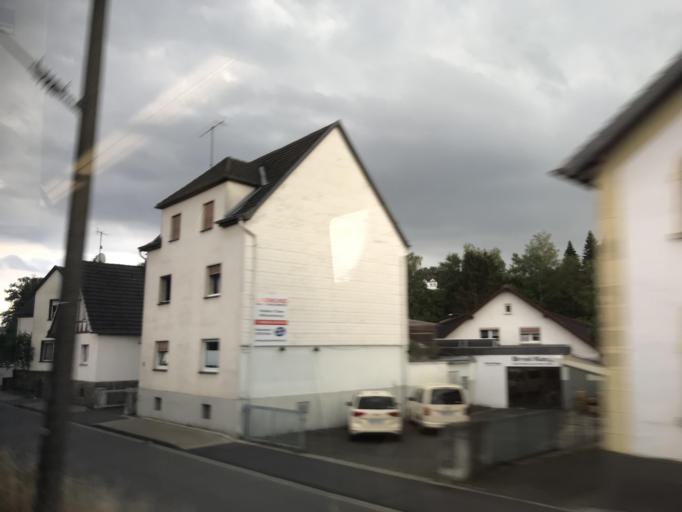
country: DE
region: North Rhine-Westphalia
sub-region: Regierungsbezirk Koln
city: Eitorf
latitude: 50.7711
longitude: 7.4588
